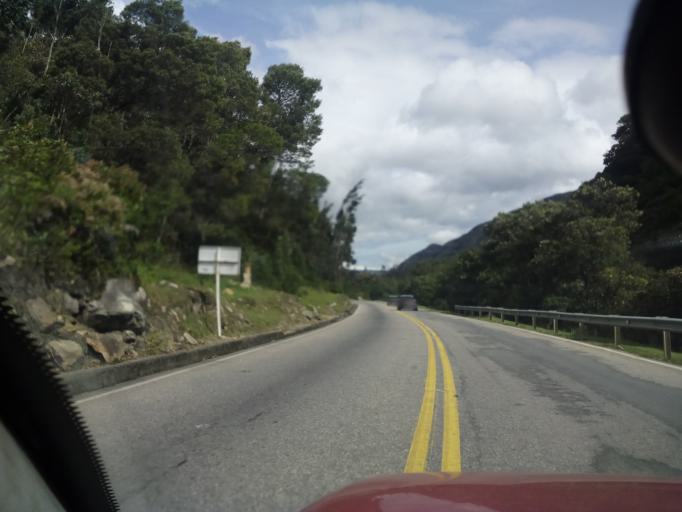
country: CO
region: Boyaca
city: Arcabuco
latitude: 5.7297
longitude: -73.3959
